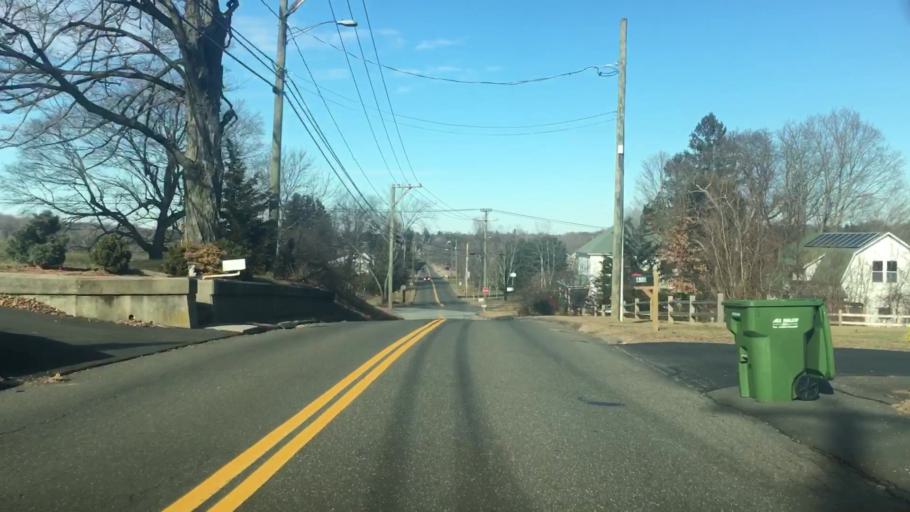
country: US
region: Connecticut
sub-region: Middlesex County
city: Middletown
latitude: 41.5200
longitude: -72.6491
